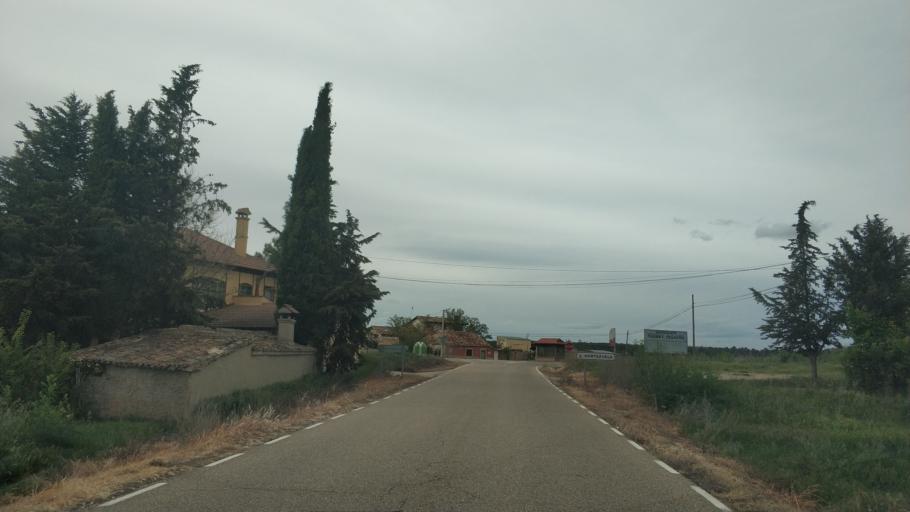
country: ES
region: Castille and Leon
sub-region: Provincia de Soria
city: Berlanga de Duero
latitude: 41.4943
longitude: -2.8688
